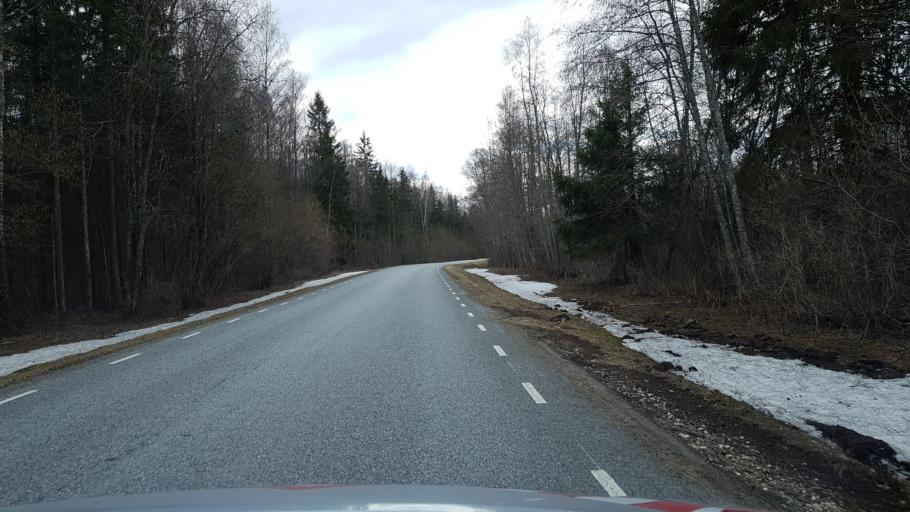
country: EE
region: Laeaene-Virumaa
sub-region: Tamsalu vald
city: Tamsalu
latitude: 59.2169
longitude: 26.1585
